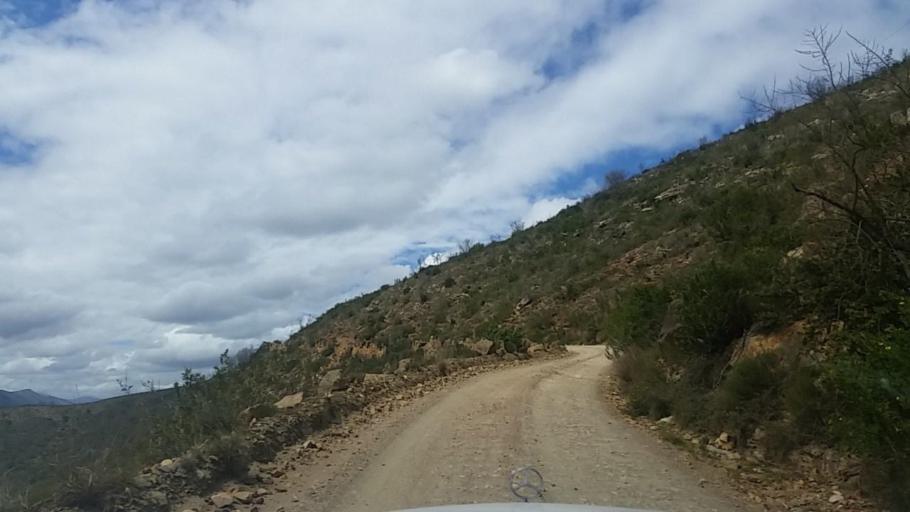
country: ZA
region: Western Cape
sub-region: Eden District Municipality
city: Knysna
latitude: -33.8239
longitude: 23.1816
